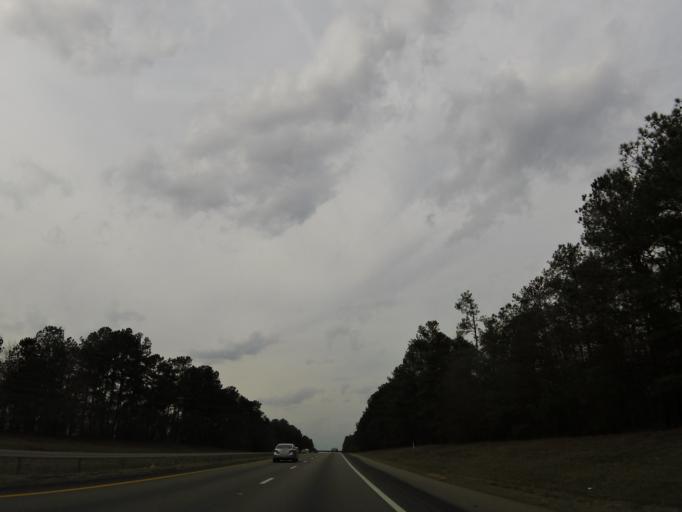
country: US
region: South Carolina
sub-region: Calhoun County
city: Oak Grove
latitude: 33.6937
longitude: -80.9120
